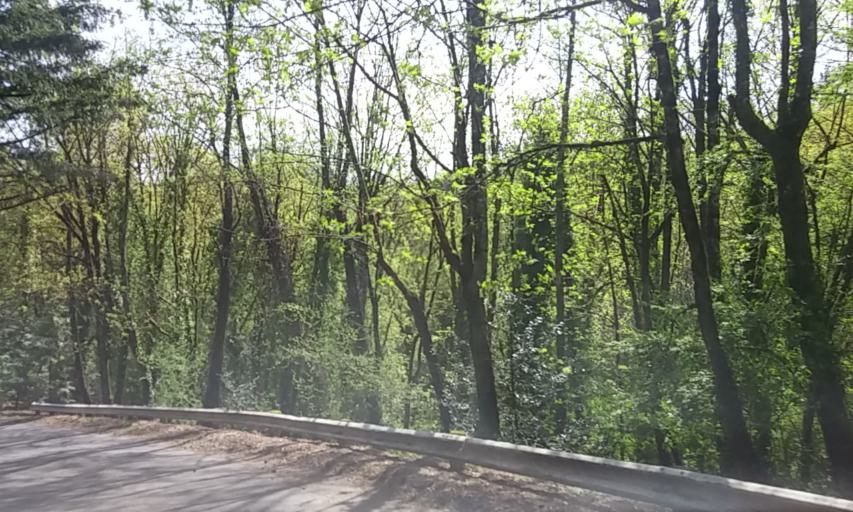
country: US
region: Oregon
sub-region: Washington County
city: West Haven-Sylvan
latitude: 45.5234
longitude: -122.7424
